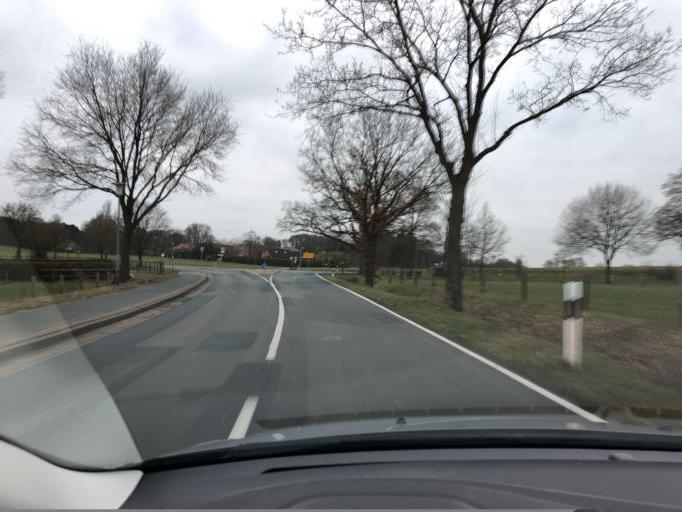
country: DE
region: Lower Saxony
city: Ganderkesee
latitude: 53.0758
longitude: 8.5575
